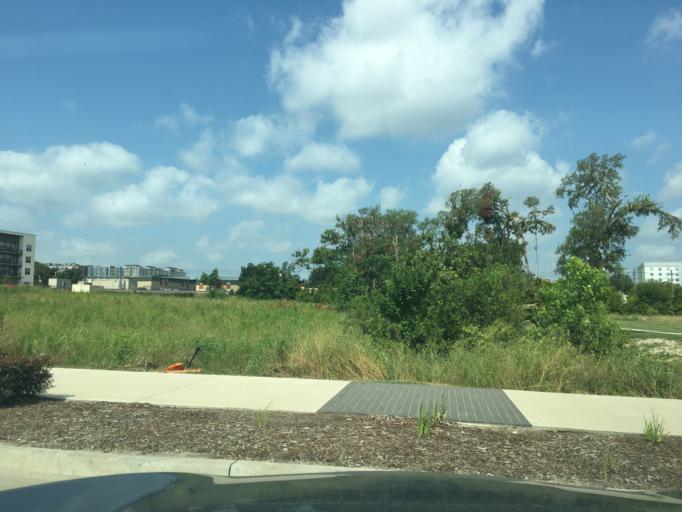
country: US
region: Texas
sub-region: Dallas County
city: University Park
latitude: 32.8903
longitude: -96.7631
